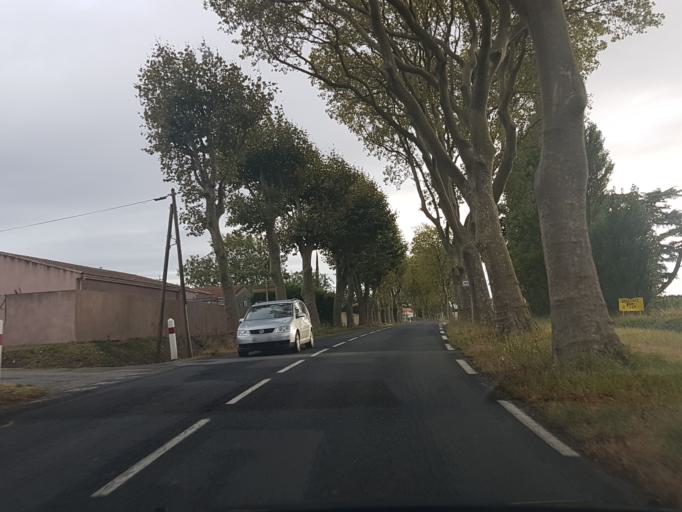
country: FR
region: Languedoc-Roussillon
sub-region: Departement de l'Aude
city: Bram
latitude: 43.2311
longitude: 2.0967
